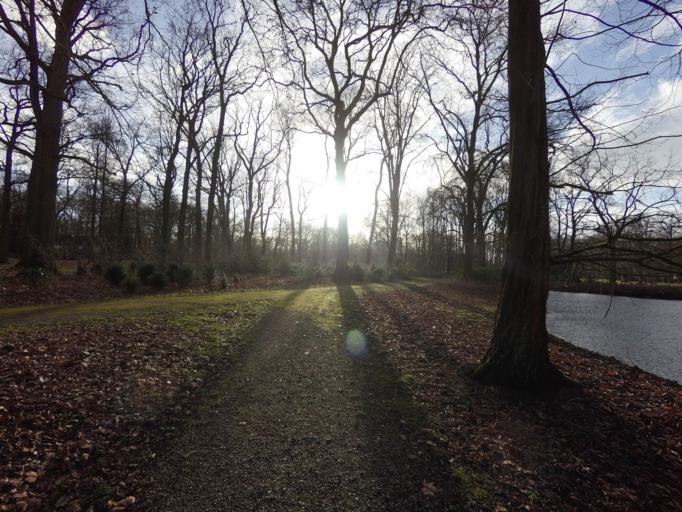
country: NL
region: Utrecht
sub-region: Stichtse Vecht
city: Spechtenkamp
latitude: 52.1240
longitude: 4.9909
